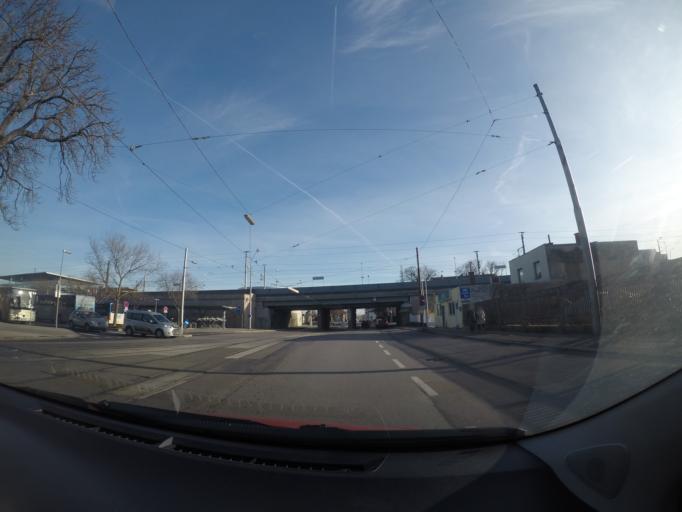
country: AT
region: Lower Austria
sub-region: Politischer Bezirk Baden
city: Baden
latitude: 48.0036
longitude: 16.2413
